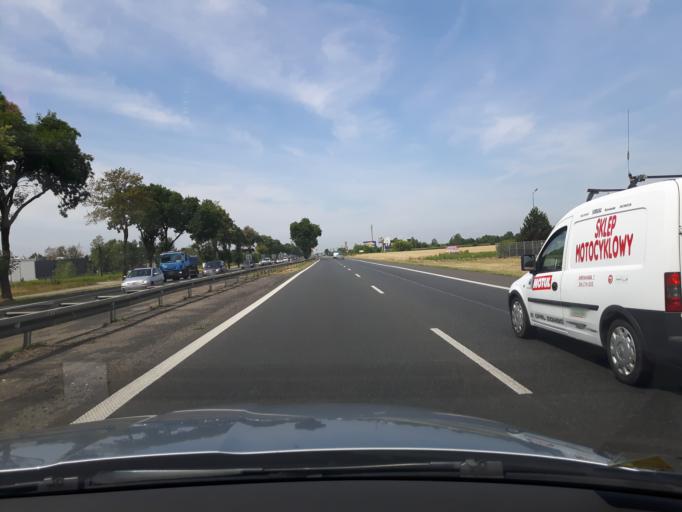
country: PL
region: Masovian Voivodeship
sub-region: Powiat warszawski zachodni
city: Dziekanow Lesny
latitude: 52.3728
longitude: 20.7880
